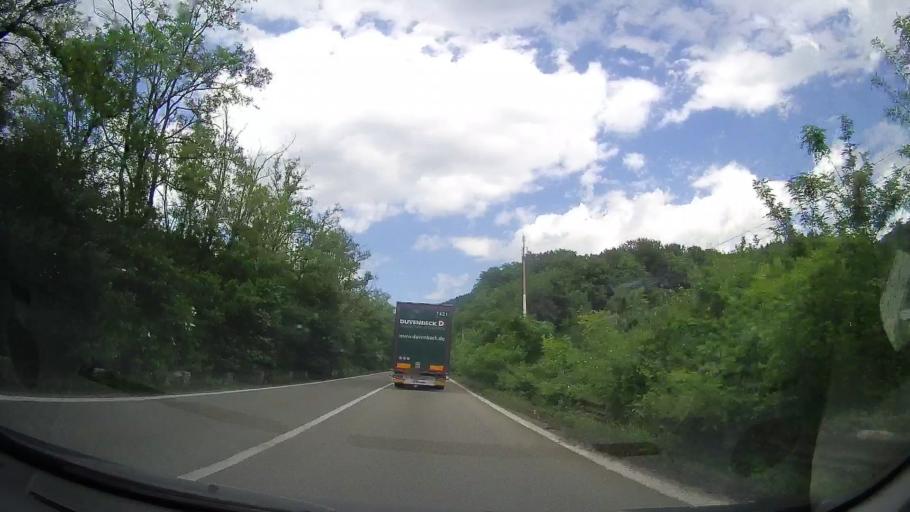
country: RO
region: Valcea
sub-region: Oras Calimanesti
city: Calimanesti
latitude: 45.2639
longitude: 24.3234
